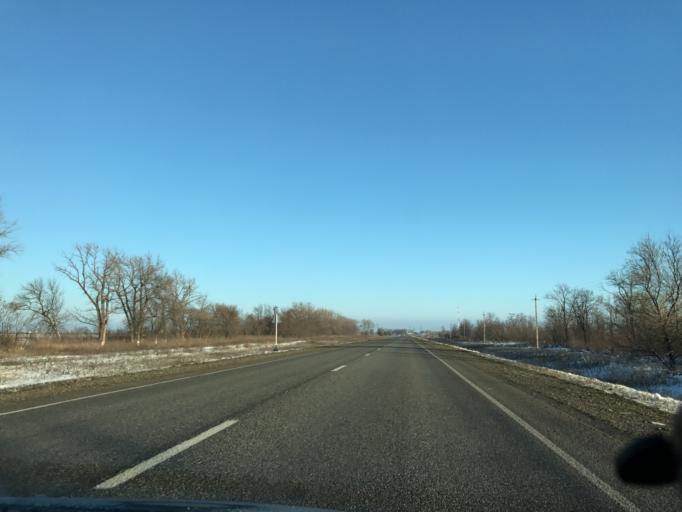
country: RU
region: Stavropol'skiy
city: Bezopasnoye
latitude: 45.6052
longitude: 41.9416
